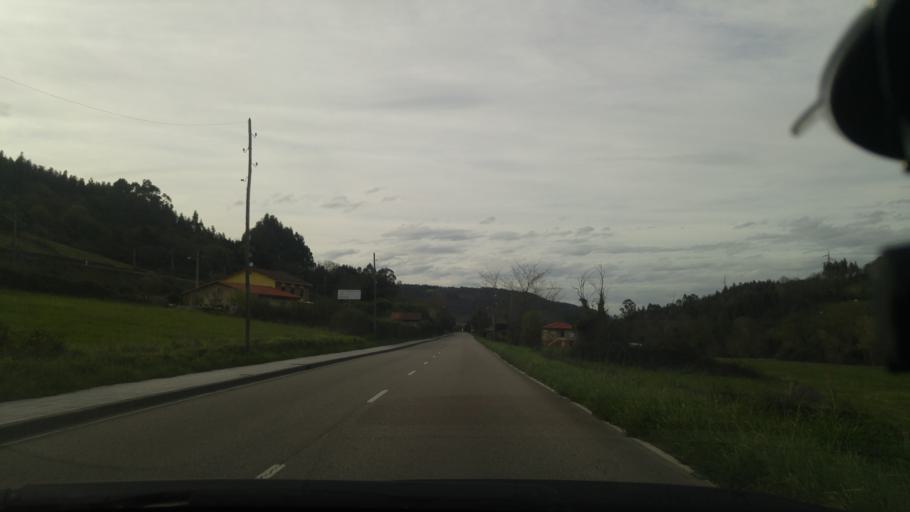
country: ES
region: Asturias
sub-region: Province of Asturias
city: Corvera de Asturias
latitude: 43.5001
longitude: -5.8599
